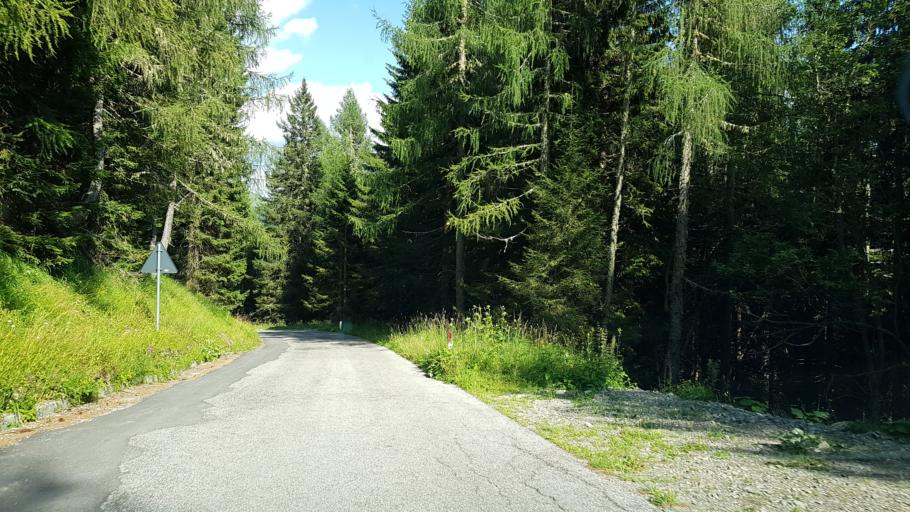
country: IT
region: Friuli Venezia Giulia
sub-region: Provincia di Udine
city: Sauris di Sotto
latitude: 46.4730
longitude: 12.6449
